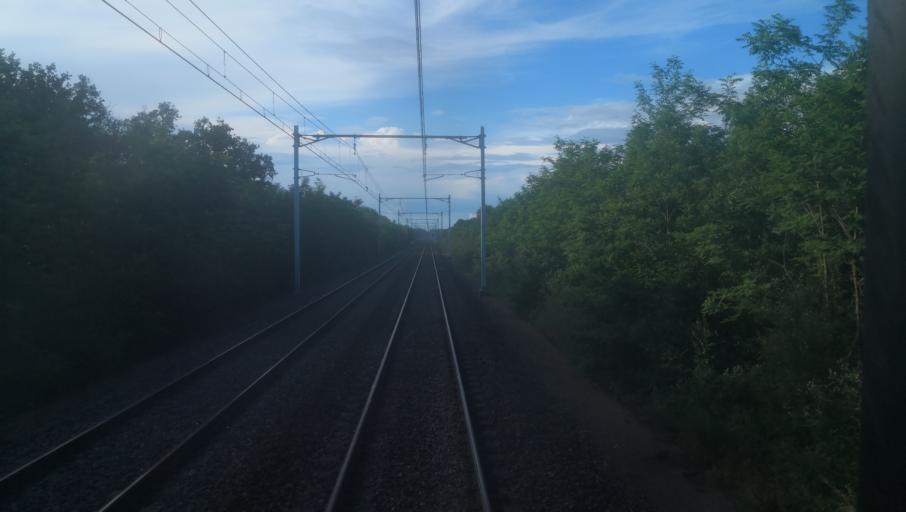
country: FR
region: Centre
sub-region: Departement du Loir-et-Cher
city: Theillay
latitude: 47.3235
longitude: 2.0450
